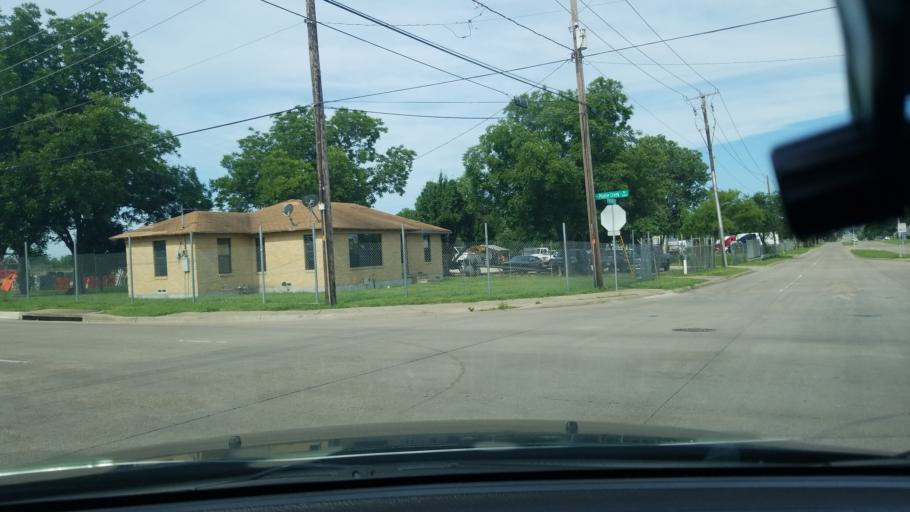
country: US
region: Texas
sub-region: Dallas County
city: Balch Springs
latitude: 32.7779
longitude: -96.6653
